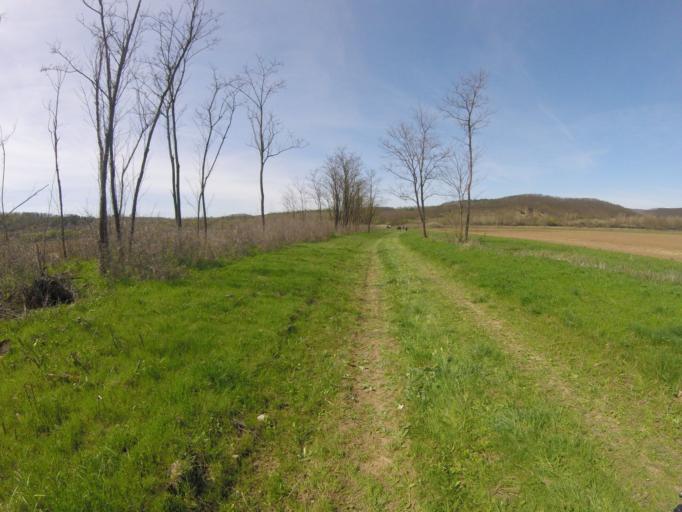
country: HU
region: Borsod-Abauj-Zemplen
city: Szendro
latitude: 48.4186
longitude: 20.7616
